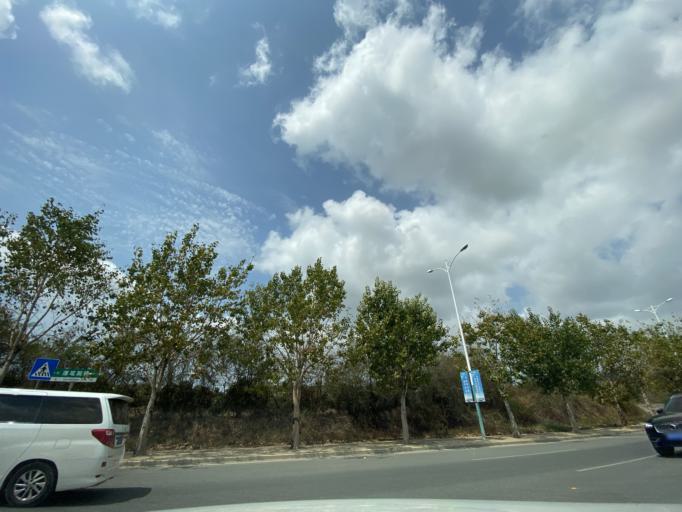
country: CN
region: Hainan
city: Tiandu
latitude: 18.3215
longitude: 109.5252
